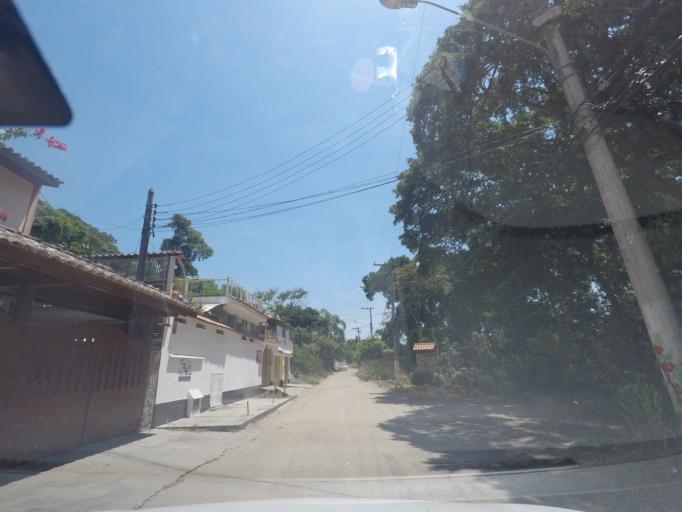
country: BR
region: Rio de Janeiro
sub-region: Niteroi
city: Niteroi
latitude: -22.9699
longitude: -43.0422
